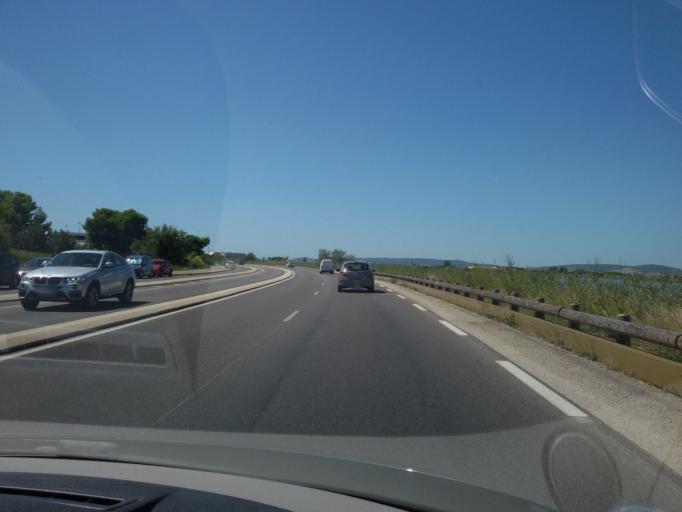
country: FR
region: Languedoc-Roussillon
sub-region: Departement de l'Herault
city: Palavas-les-Flots
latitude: 43.5352
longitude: 3.9301
